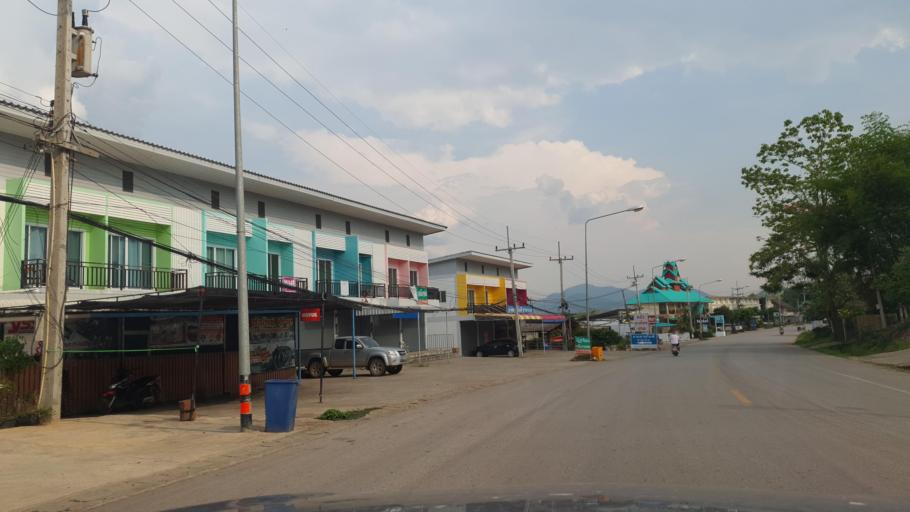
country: TH
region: Chiang Mai
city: Pai
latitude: 19.3518
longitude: 98.4353
